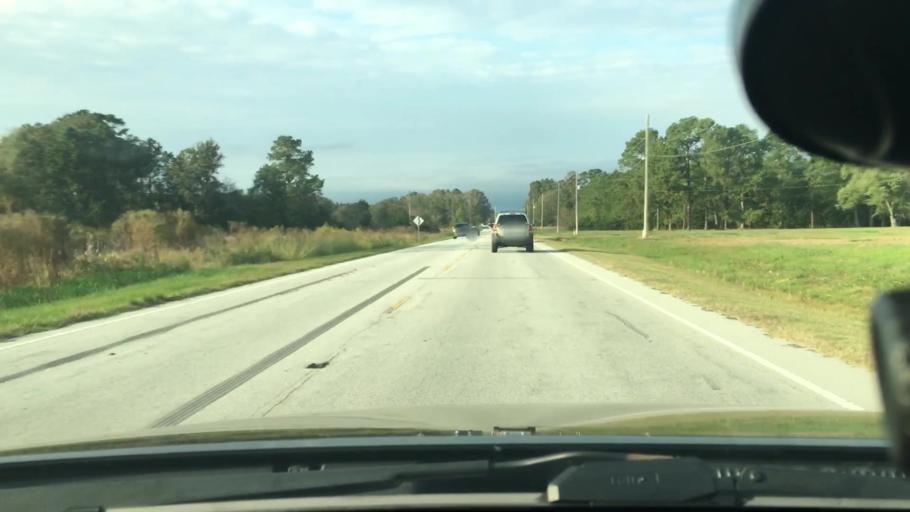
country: US
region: North Carolina
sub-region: Pitt County
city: Windsor
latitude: 35.5193
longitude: -77.3192
